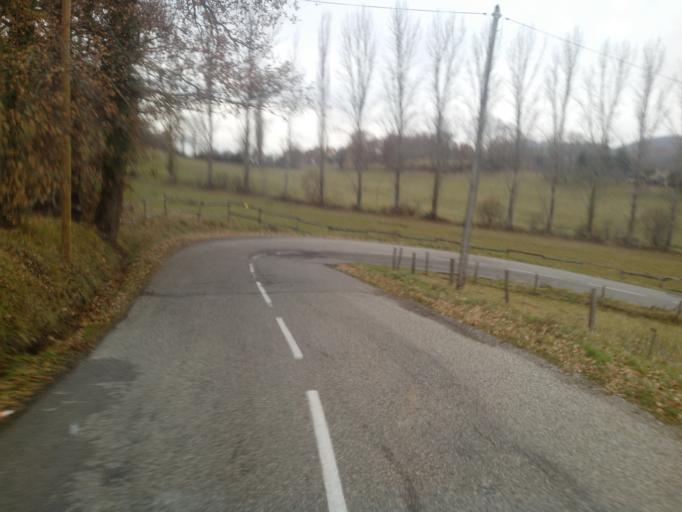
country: FR
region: Midi-Pyrenees
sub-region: Departement de l'Ariege
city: Varilhes
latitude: 43.0365
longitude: 1.5361
